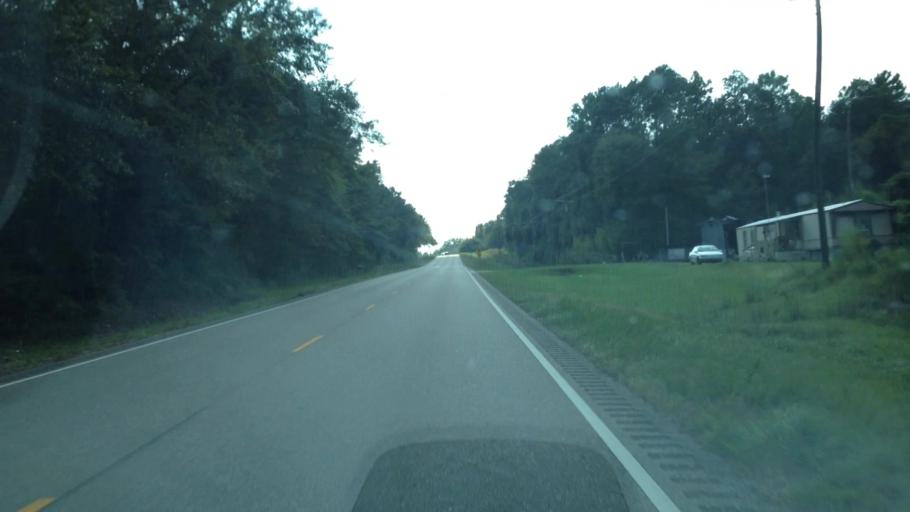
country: US
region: Florida
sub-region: Okaloosa County
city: Crestview
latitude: 31.0356
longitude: -86.6039
